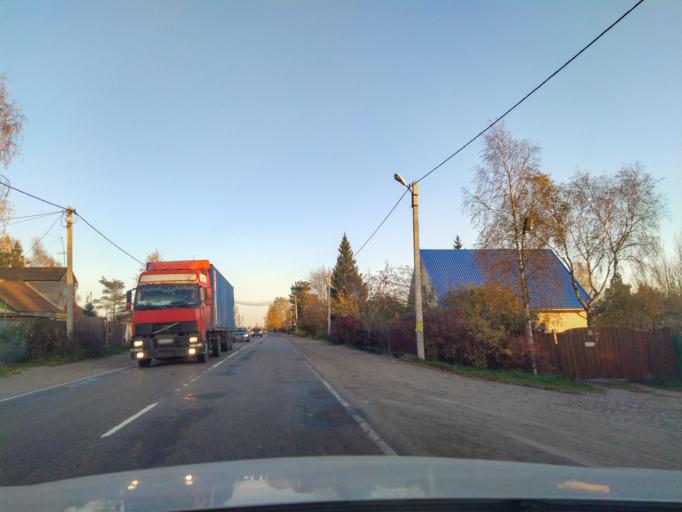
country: RU
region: Leningrad
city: Maloye Verevo
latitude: 59.6141
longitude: 30.2195
